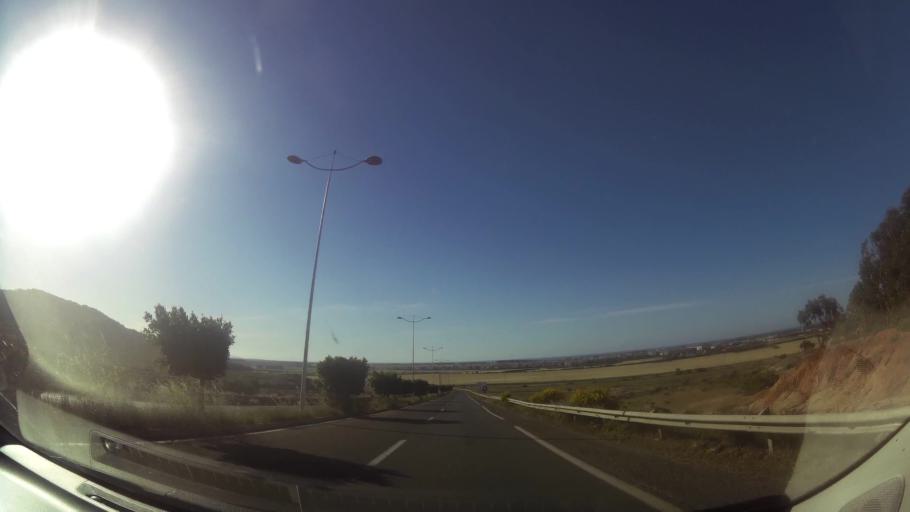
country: MA
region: Oriental
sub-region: Berkane-Taourirt
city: Madagh
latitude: 35.0607
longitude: -2.2234
